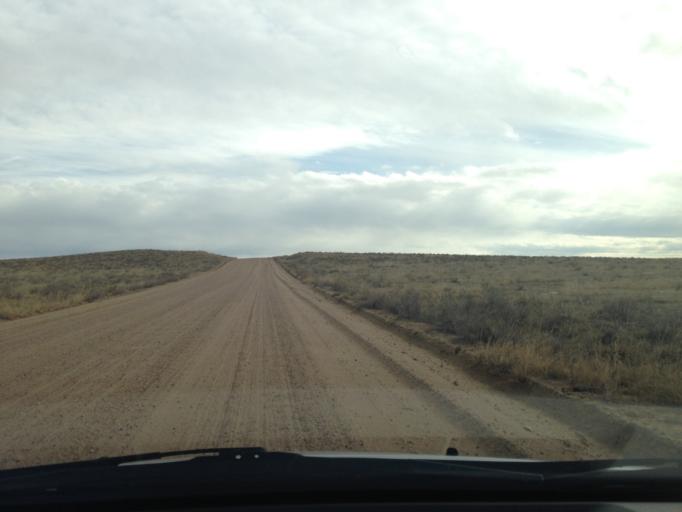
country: US
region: Colorado
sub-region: Weld County
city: Keenesburg
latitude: 40.2527
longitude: -104.2068
